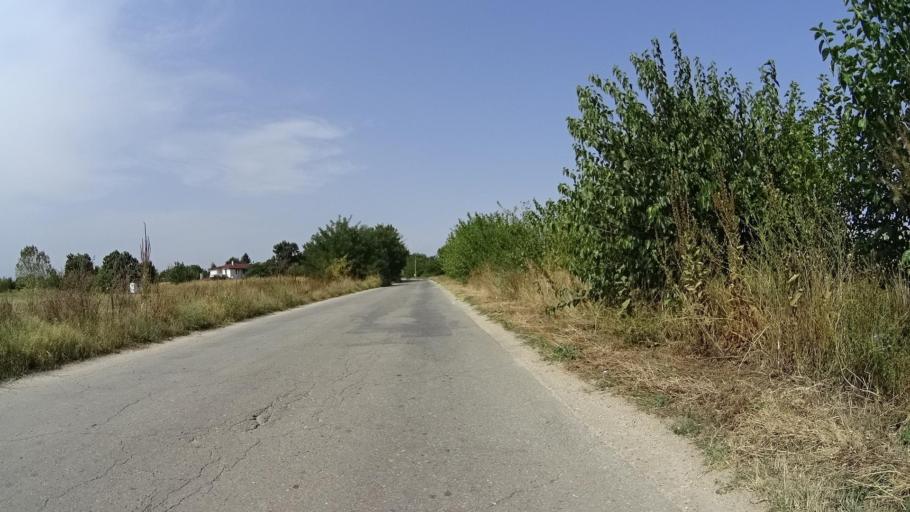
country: BG
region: Plovdiv
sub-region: Obshtina Kaloyanovo
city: Kaloyanovo
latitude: 42.2626
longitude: 24.8009
